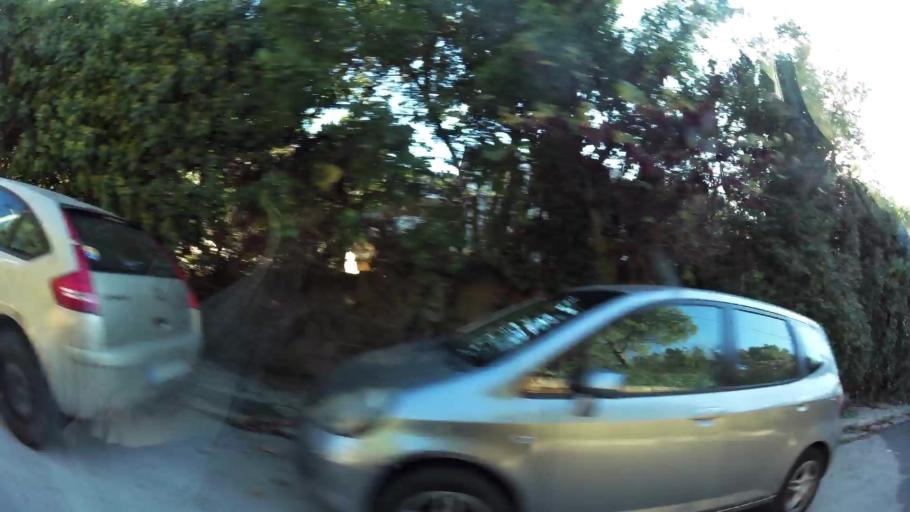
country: GR
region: Attica
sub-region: Nomarchia Athinas
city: Ekali
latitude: 38.1056
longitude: 23.8417
